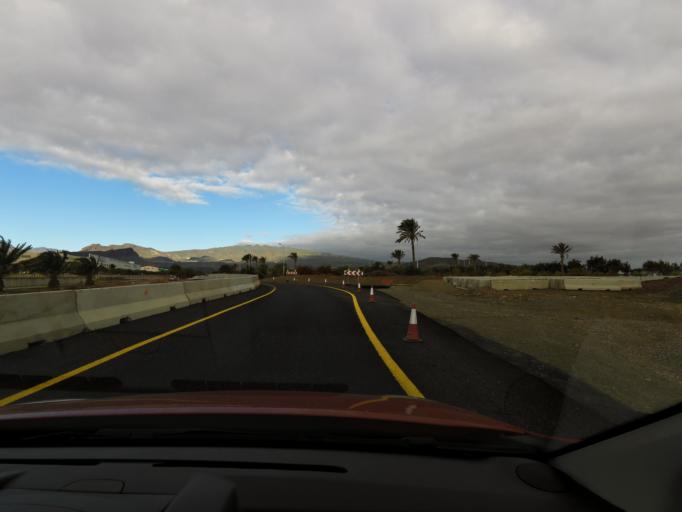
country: ES
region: Canary Islands
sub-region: Provincia de Las Palmas
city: Cruce de Arinaga
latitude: 27.8668
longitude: -15.4235
